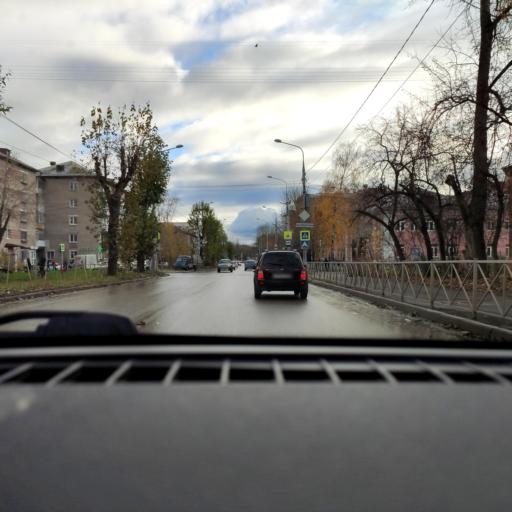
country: RU
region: Perm
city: Perm
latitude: 57.9665
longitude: 56.2316
